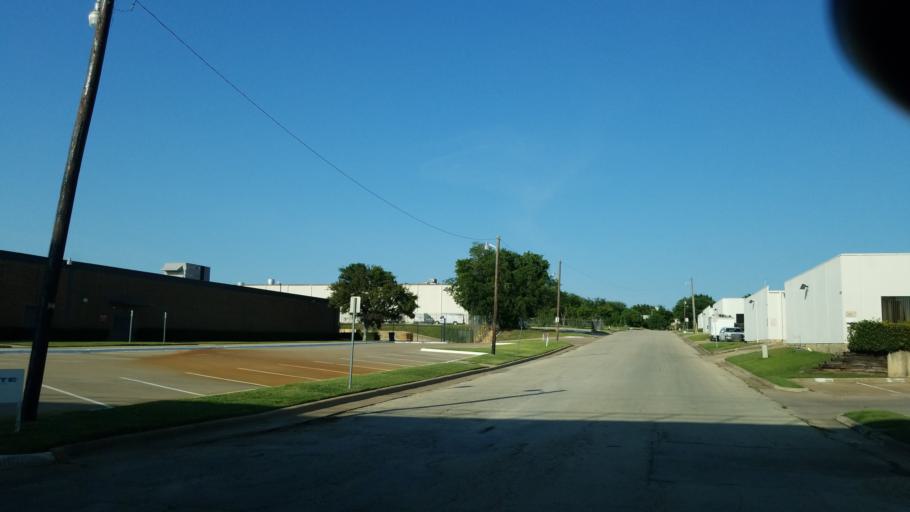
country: US
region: Texas
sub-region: Dallas County
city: Carrollton
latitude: 32.9447
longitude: -96.9014
